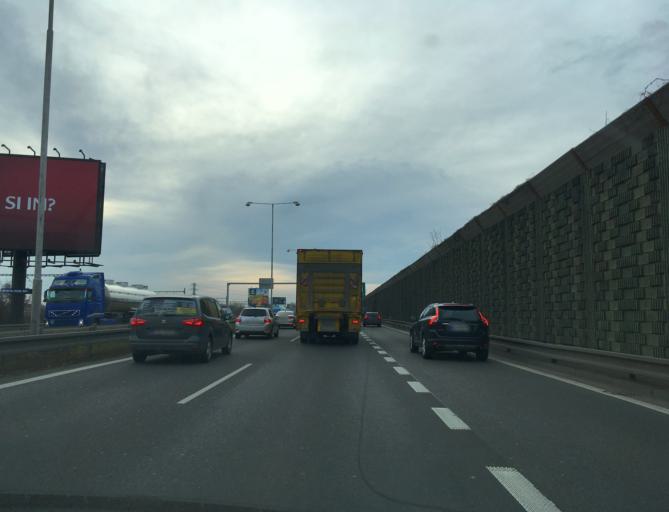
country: SK
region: Bratislavsky
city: Bratislava
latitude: 48.1418
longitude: 17.1627
